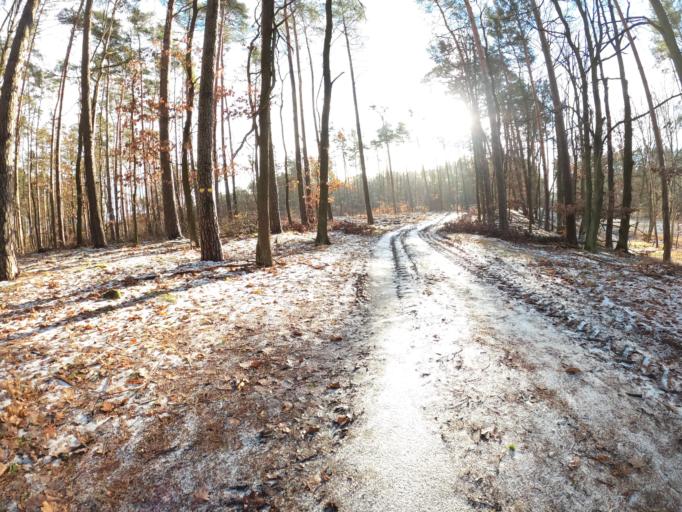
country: PL
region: Lubusz
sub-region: Powiat slubicki
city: Rzepin
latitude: 52.3006
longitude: 14.8134
